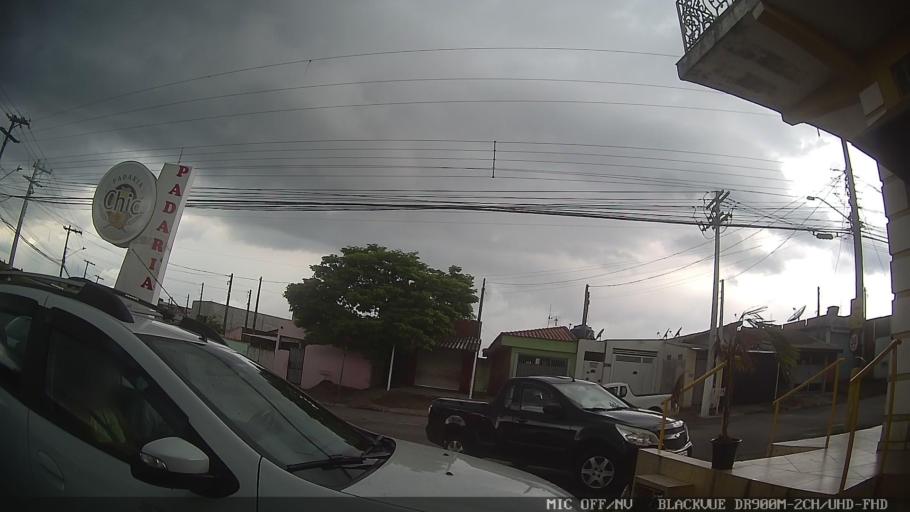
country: BR
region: Sao Paulo
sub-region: Atibaia
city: Atibaia
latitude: -23.1433
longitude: -46.5874
